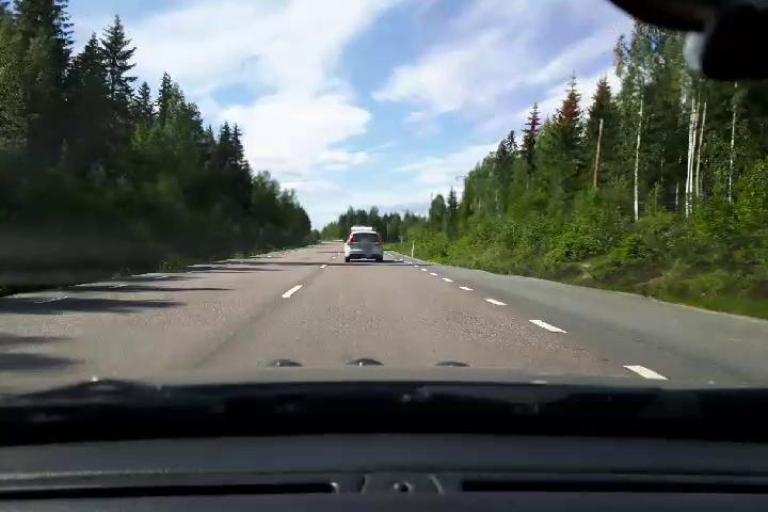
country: SE
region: Gaevleborg
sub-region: Bollnas Kommun
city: Kilafors
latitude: 61.2865
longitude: 16.5131
